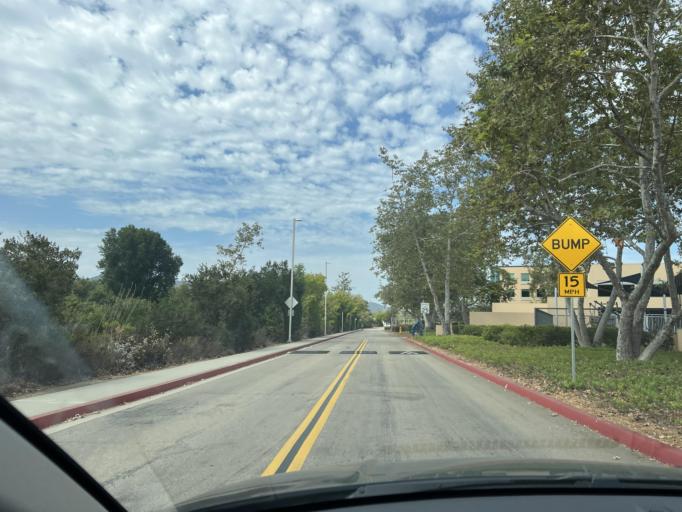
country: US
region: California
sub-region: San Diego County
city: San Marcos
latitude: 33.1407
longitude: -117.1591
